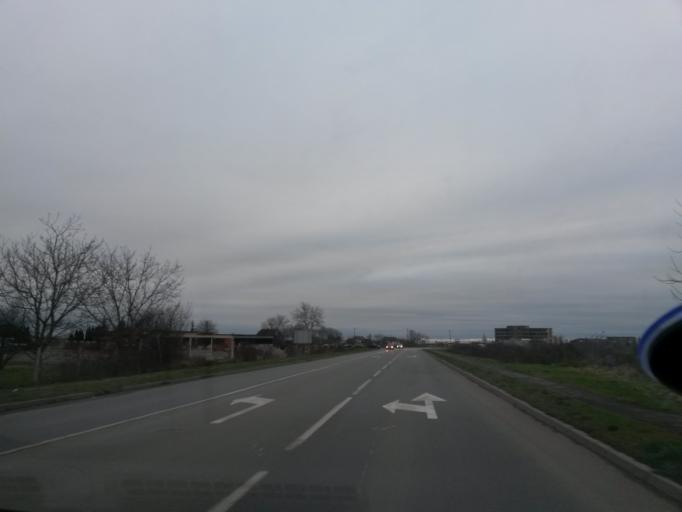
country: HR
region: Osjecko-Baranjska
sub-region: Grad Osijek
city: Osijek
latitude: 45.5379
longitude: 18.7125
